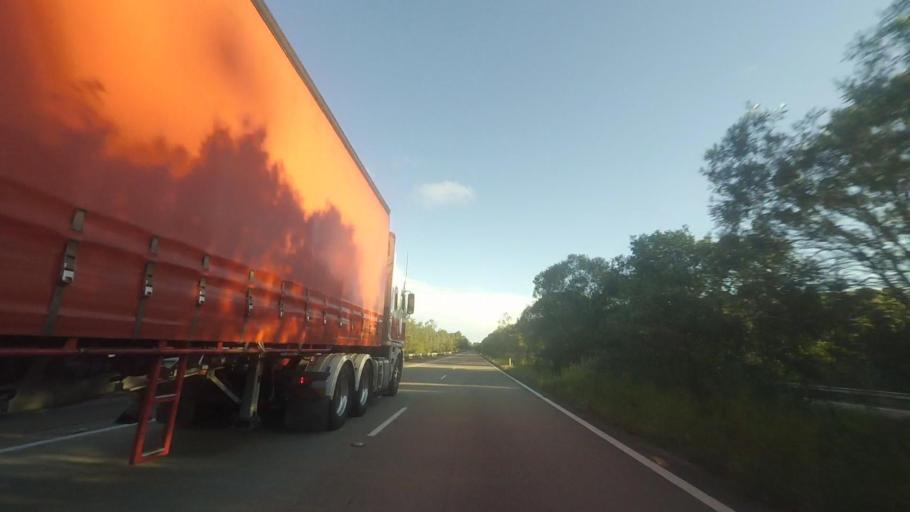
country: AU
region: New South Wales
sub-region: Great Lakes
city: Bulahdelah
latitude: -32.2899
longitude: 152.3422
